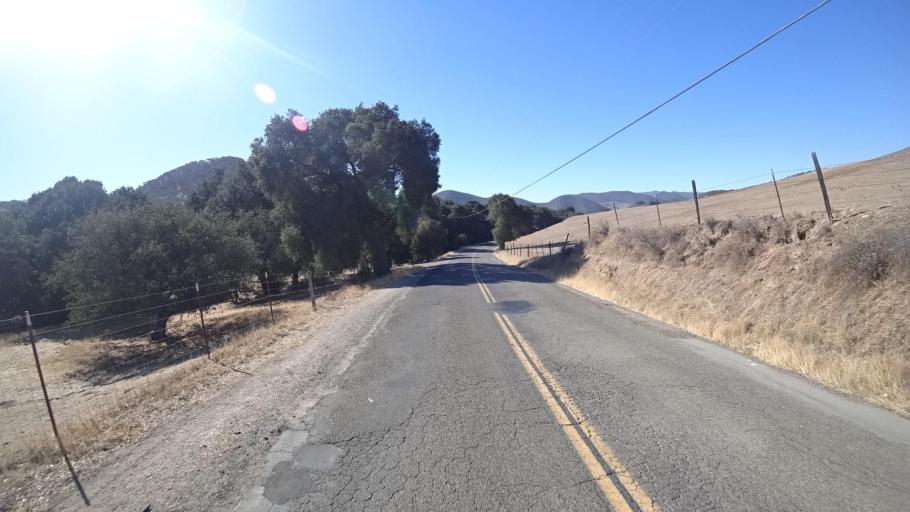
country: US
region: California
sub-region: Monterey County
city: King City
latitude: 36.1744
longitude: -121.1539
